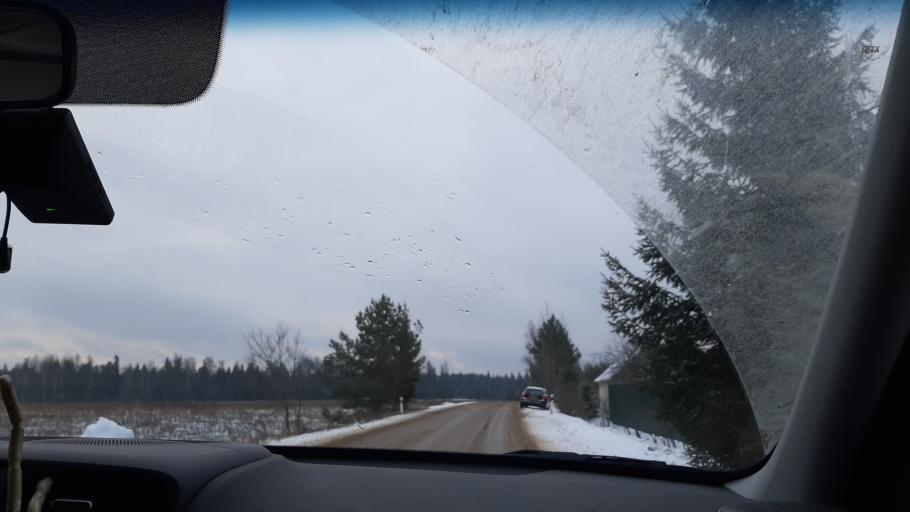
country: RU
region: Ivanovo
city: Kokhma
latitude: 56.9094
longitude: 41.0084
